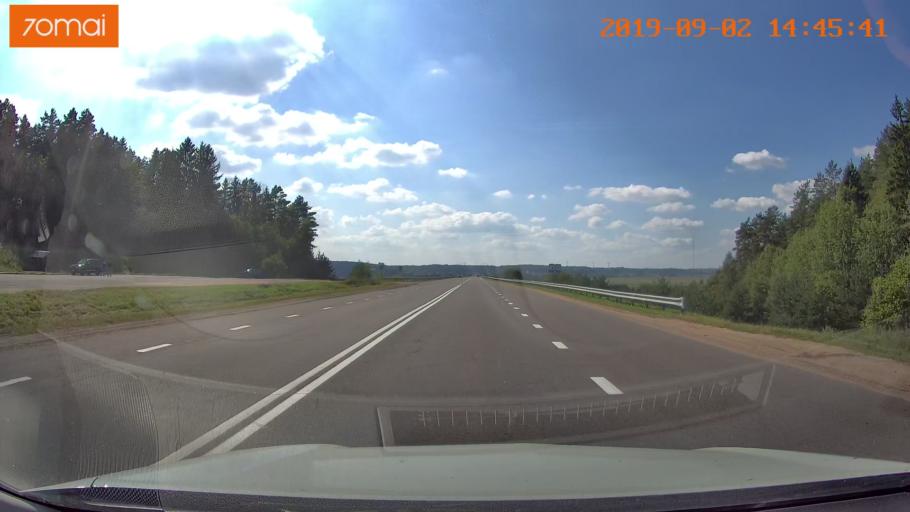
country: BY
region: Mogilev
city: Palykavichy Pyershyya
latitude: 53.9816
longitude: 30.3983
